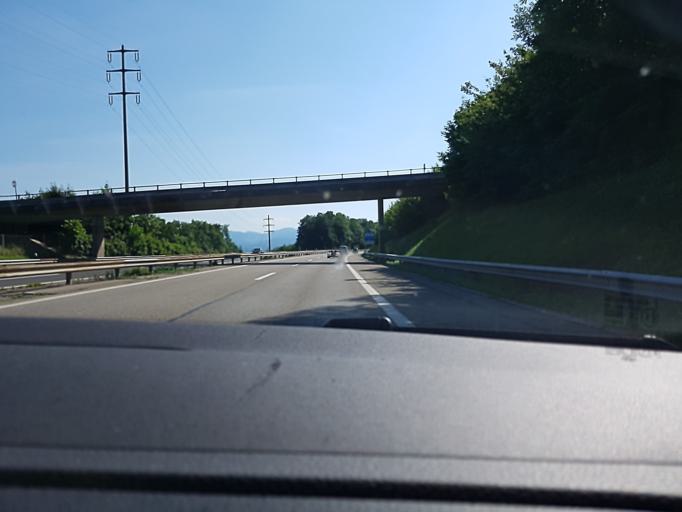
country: CH
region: Schwyz
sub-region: Bezirk Hoefe
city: Feusisberg
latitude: 47.1933
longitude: 8.7395
